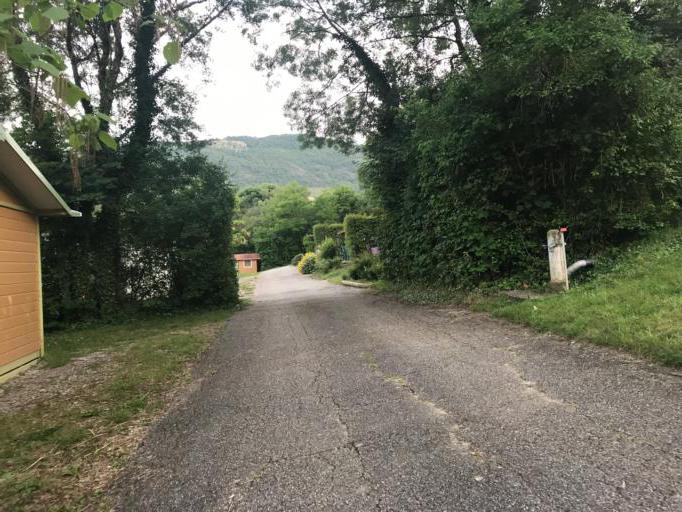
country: FR
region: Rhone-Alpes
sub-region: Departement de l'Ardeche
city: Privas
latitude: 44.7240
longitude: 4.5975
